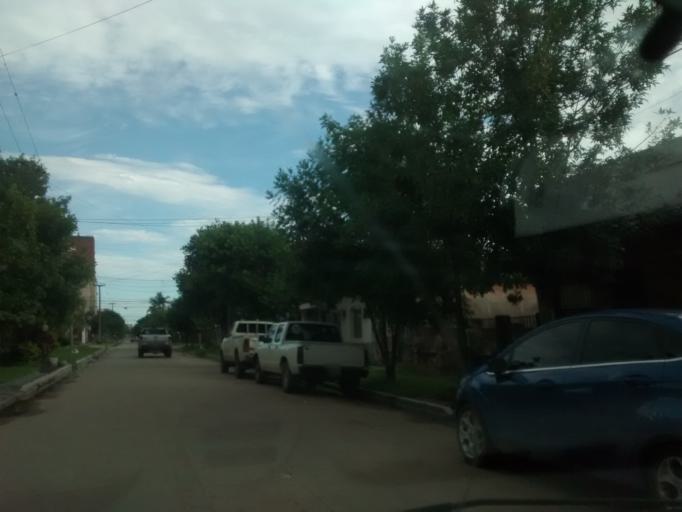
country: AR
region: Chaco
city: Resistencia
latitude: -27.4546
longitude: -58.9985
